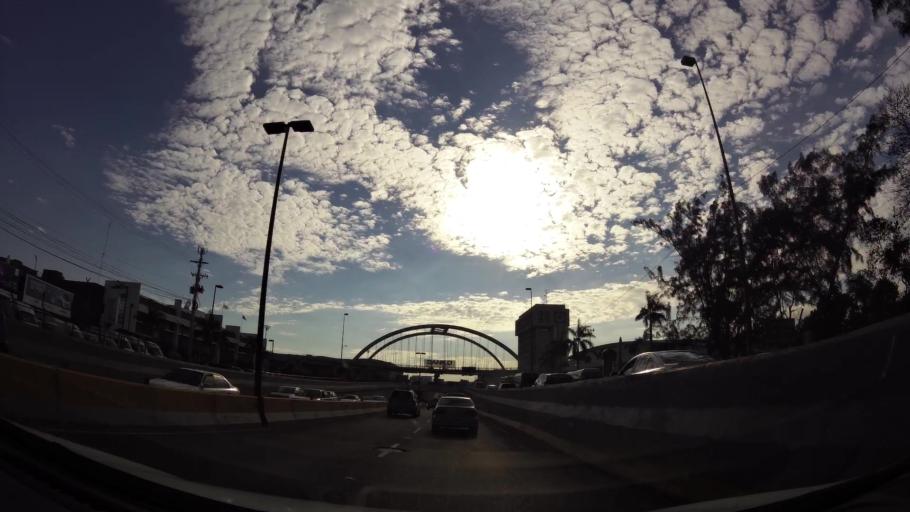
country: DO
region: Nacional
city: San Carlos
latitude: 18.4819
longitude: -69.9159
